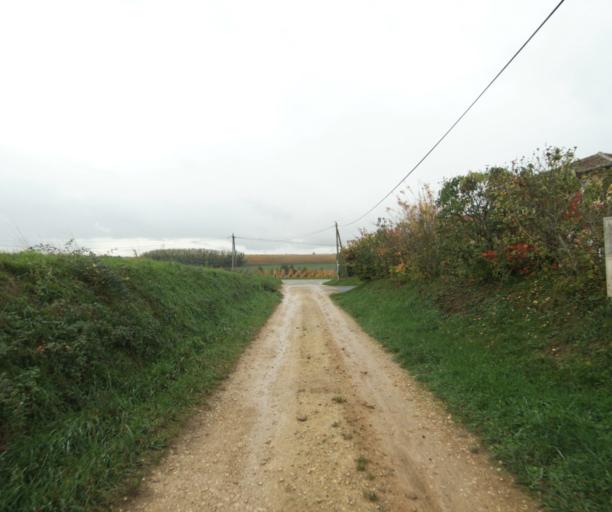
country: FR
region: Rhone-Alpes
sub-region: Departement de l'Ain
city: Pont-de-Vaux
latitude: 46.4772
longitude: 4.8662
